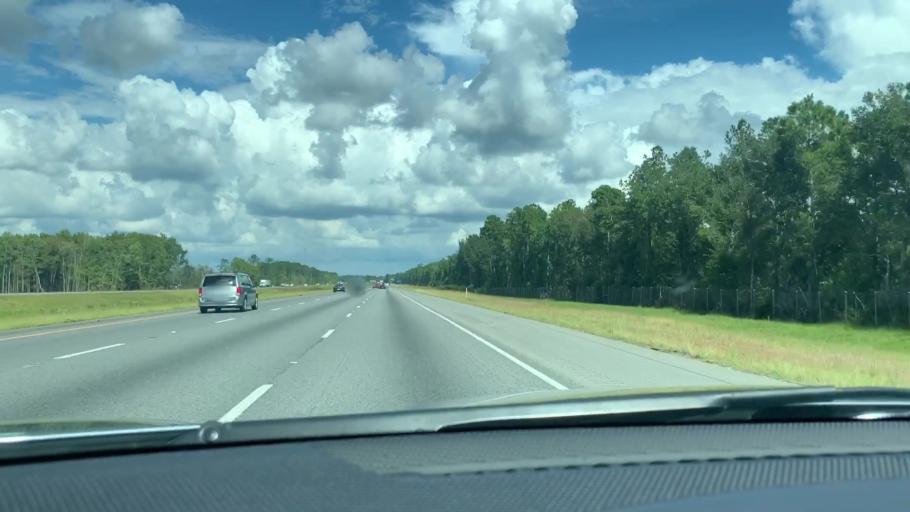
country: US
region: Georgia
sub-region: Glynn County
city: Brunswick
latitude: 31.0764
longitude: -81.6187
